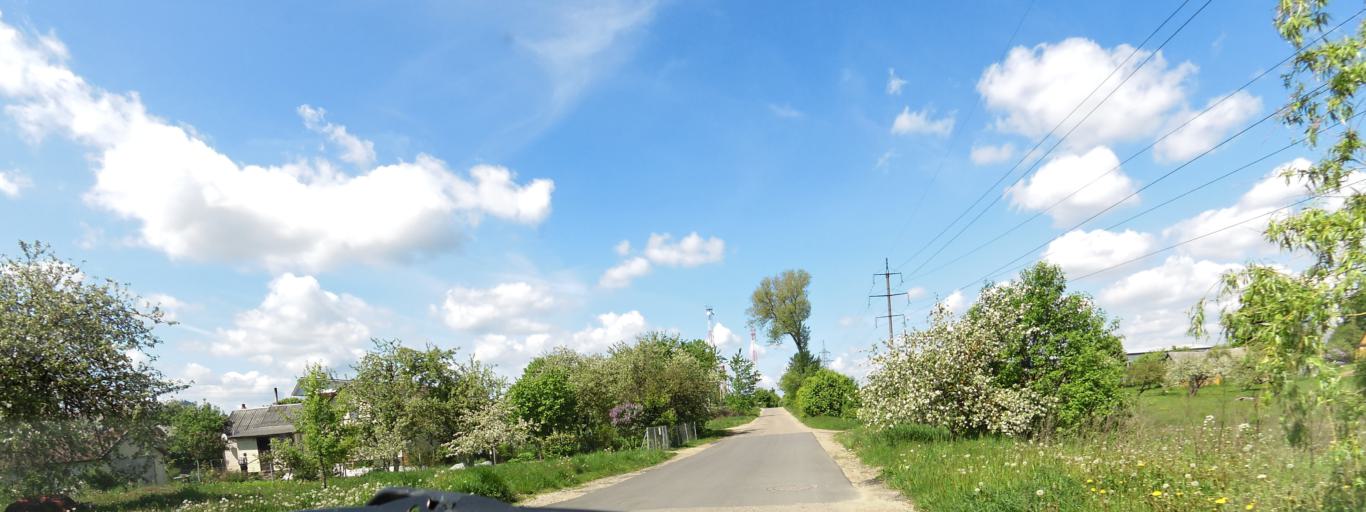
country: LT
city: Lentvaris
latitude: 54.6408
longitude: 25.0636
